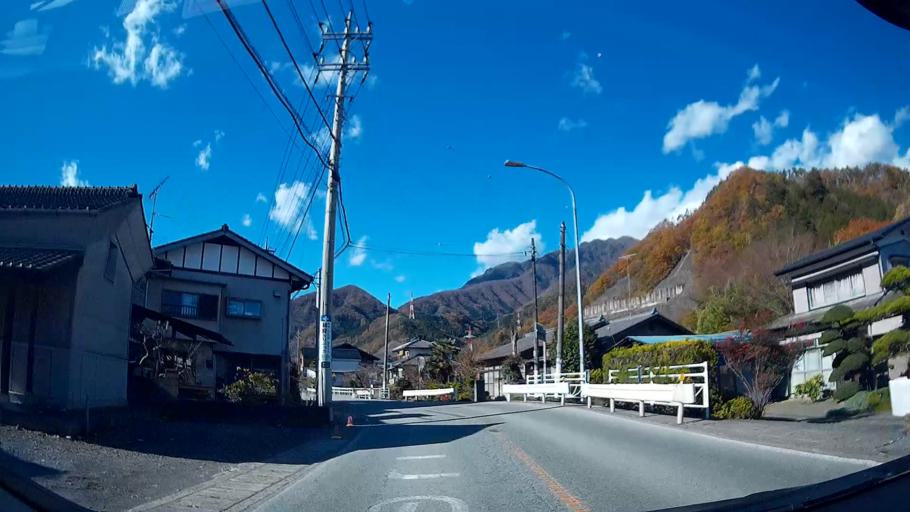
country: JP
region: Yamanashi
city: Otsuki
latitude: 35.5984
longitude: 138.8715
